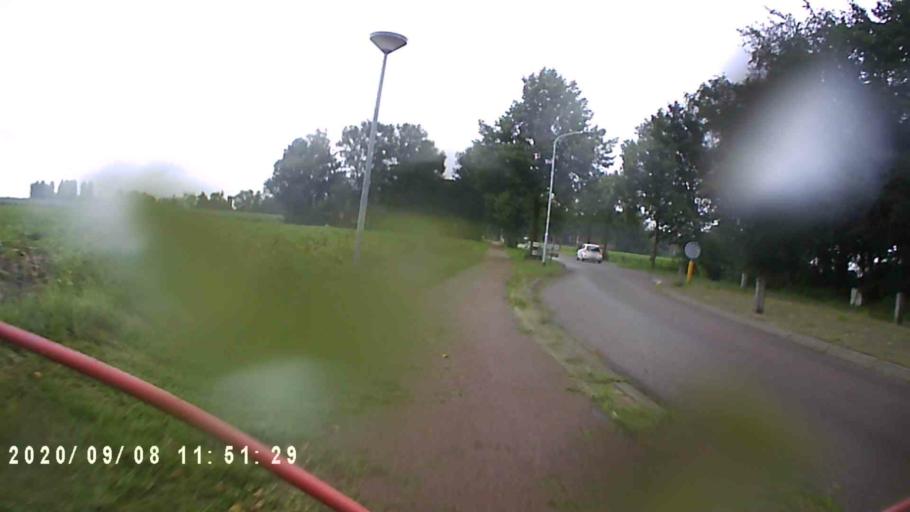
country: NL
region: Groningen
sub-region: Gemeente Hoogezand-Sappemeer
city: Sappemeer
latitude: 53.1281
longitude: 6.8112
